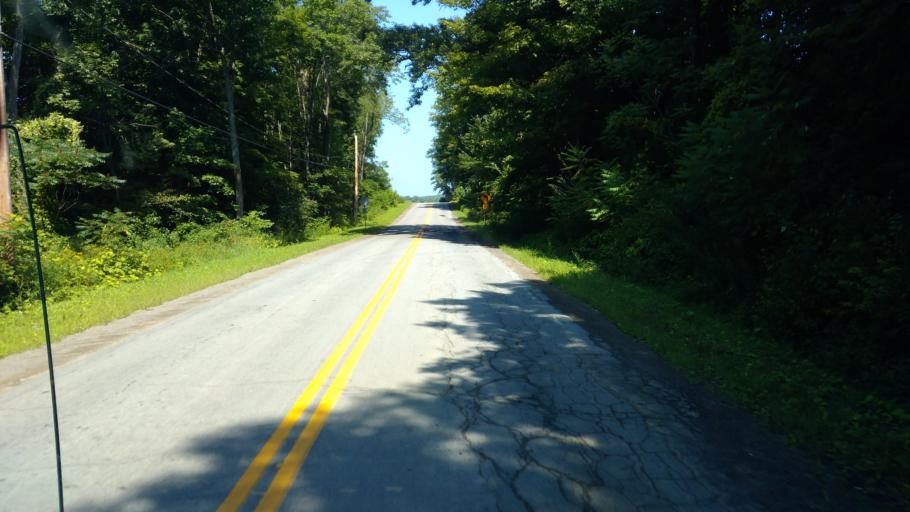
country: US
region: New York
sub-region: Allegany County
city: Belmont
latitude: 42.2895
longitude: -78.0529
